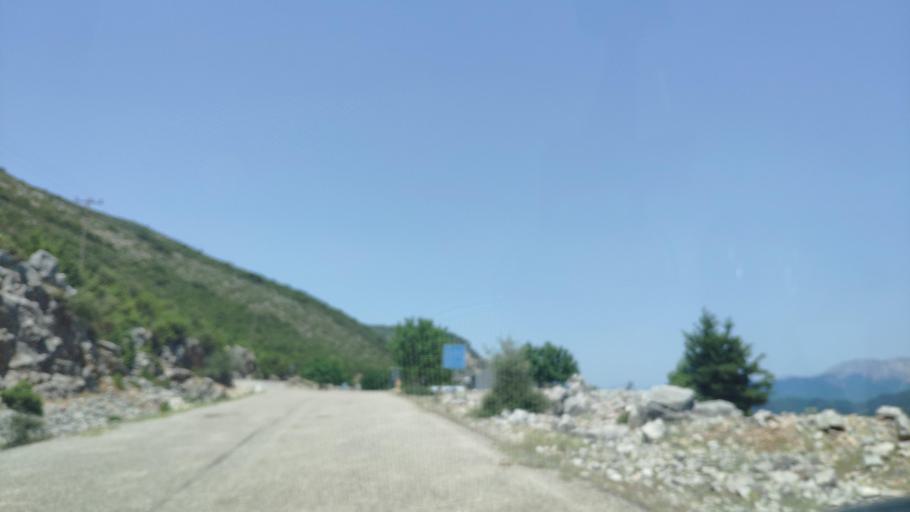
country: GR
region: Thessaly
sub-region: Nomos Kardhitsas
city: Anthiro
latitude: 39.1335
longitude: 21.3919
